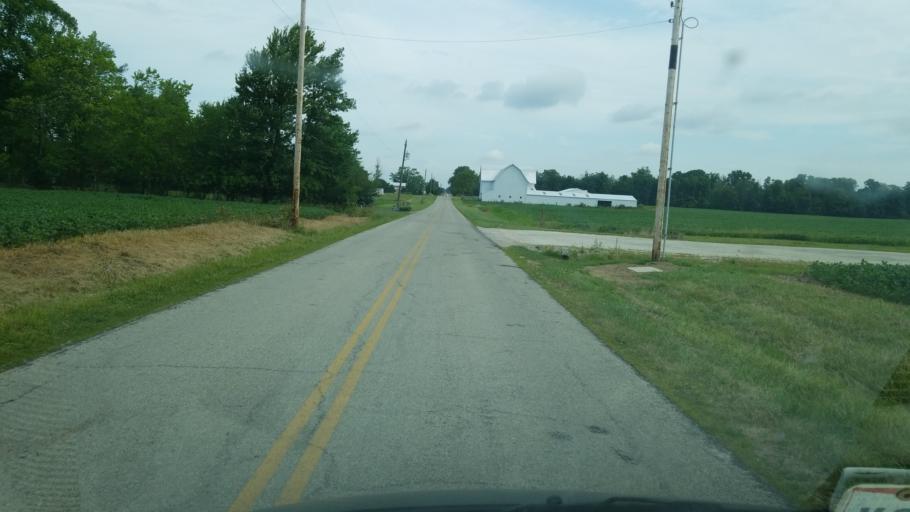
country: US
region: Ohio
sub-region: Seneca County
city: Tiffin
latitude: 41.0839
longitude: -83.0930
